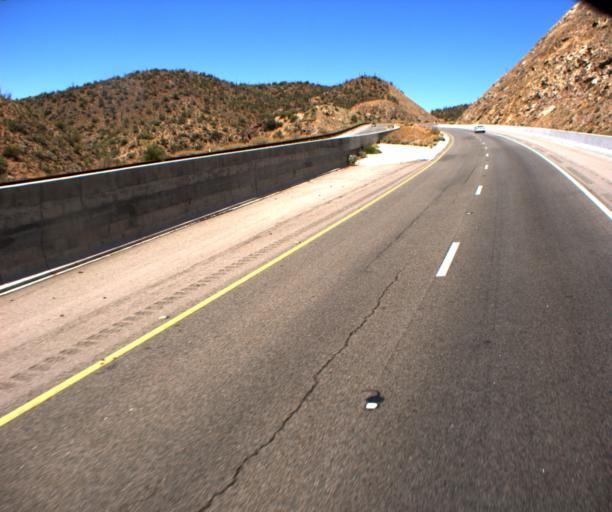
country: US
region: Arizona
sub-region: Yavapai County
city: Bagdad
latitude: 34.4048
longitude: -113.2221
